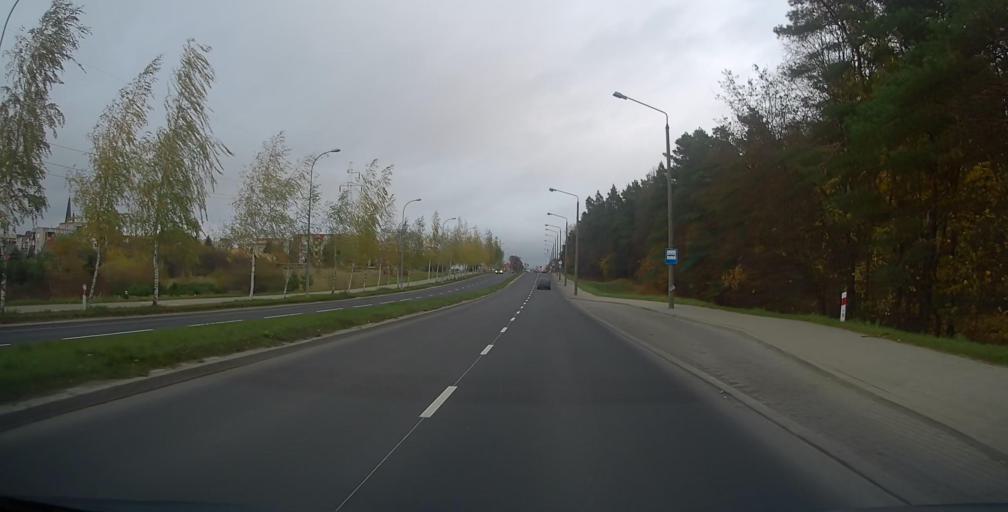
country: PL
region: Warmian-Masurian Voivodeship
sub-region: Powiat elcki
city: Elk
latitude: 53.7998
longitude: 22.3619
